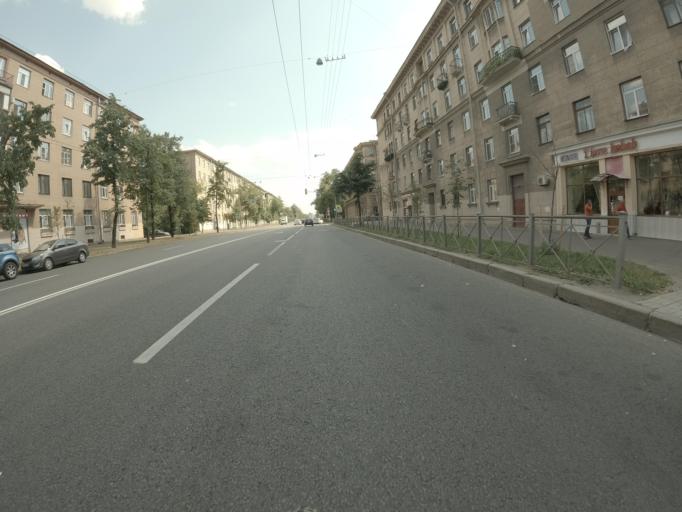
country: RU
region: St.-Petersburg
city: Avtovo
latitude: 59.8712
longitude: 30.2679
